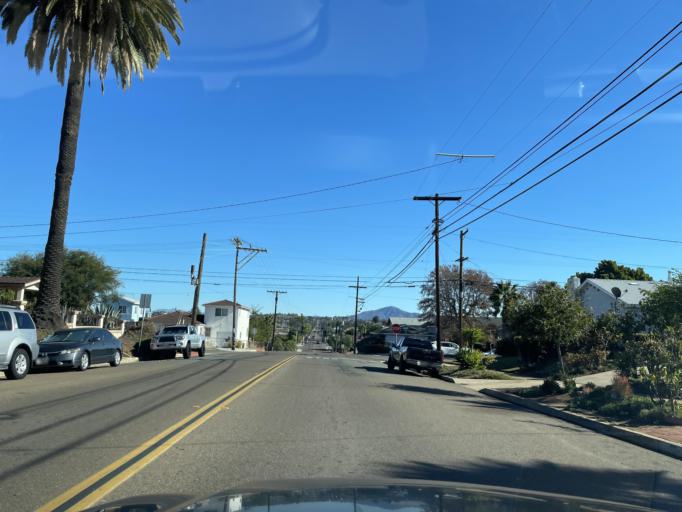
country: US
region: California
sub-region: San Diego County
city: National City
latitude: 32.6722
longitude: -117.0925
